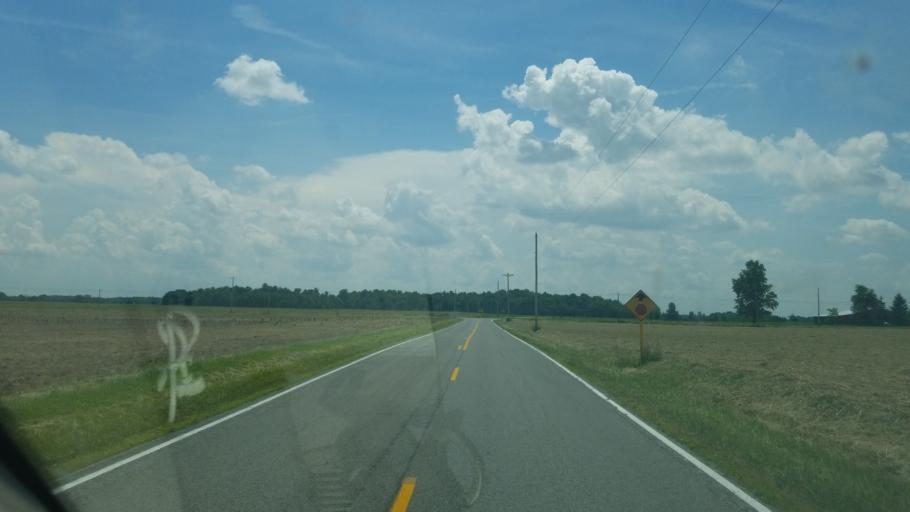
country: US
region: Ohio
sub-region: Hancock County
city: Arlington
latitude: 40.8933
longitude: -83.5948
